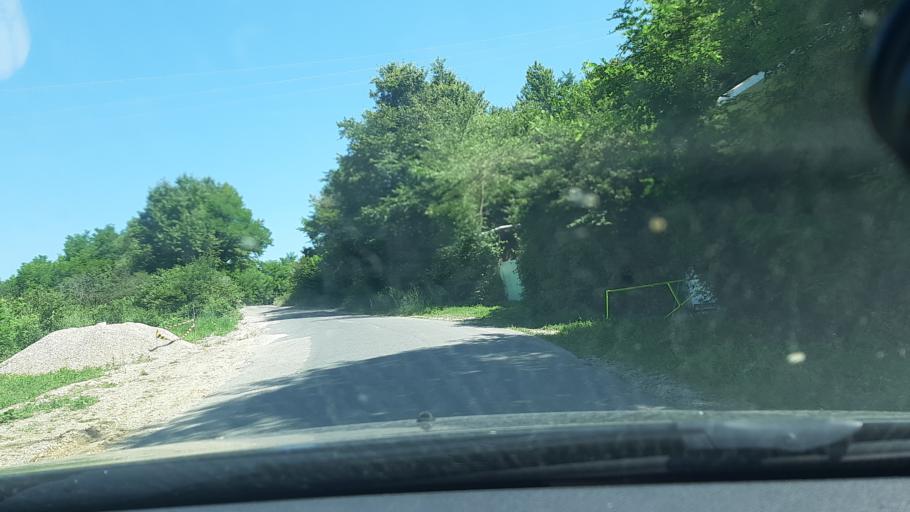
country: RO
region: Hunedoara
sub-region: Comuna Teliucu Inferior
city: Teliucu Inferior
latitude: 45.6860
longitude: 22.8736
